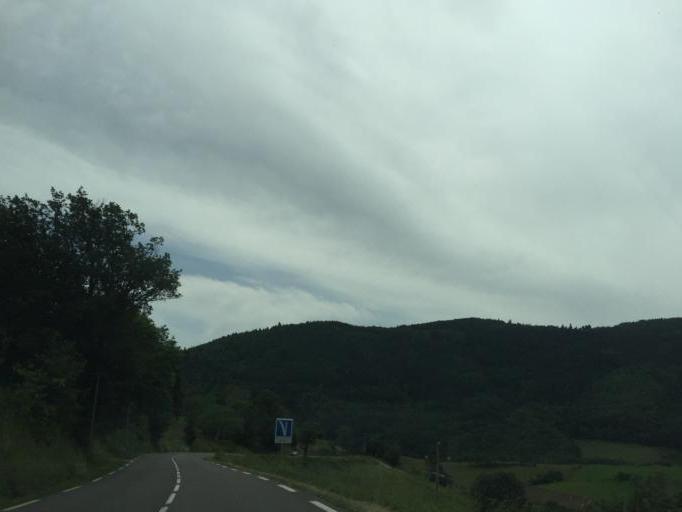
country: FR
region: Rhone-Alpes
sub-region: Departement de la Loire
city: Bourg-Argental
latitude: 45.2950
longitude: 4.5445
